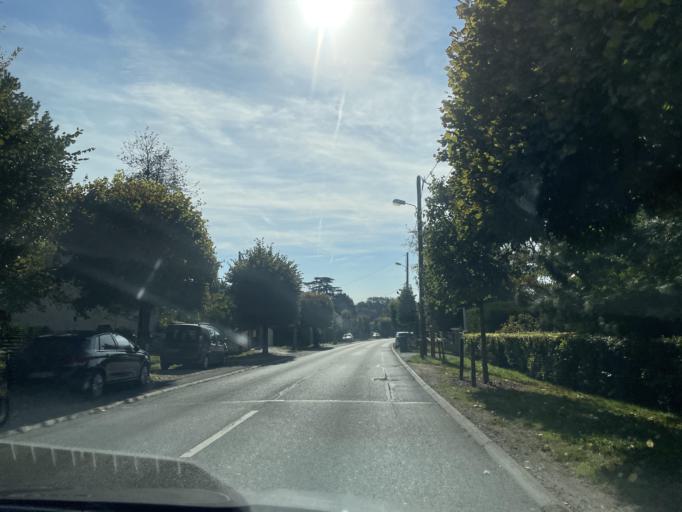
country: FR
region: Ile-de-France
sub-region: Departement de Seine-et-Marne
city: Coulommiers
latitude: 48.8245
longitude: 3.0880
